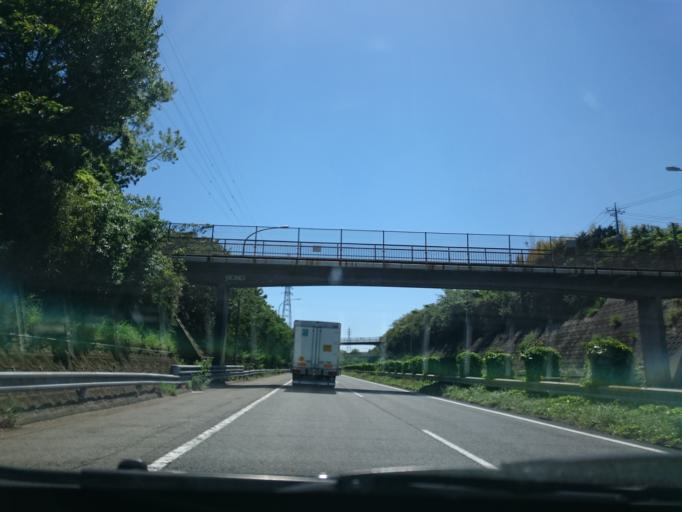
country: JP
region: Shizuoka
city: Mishima
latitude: 35.1630
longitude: 138.8885
